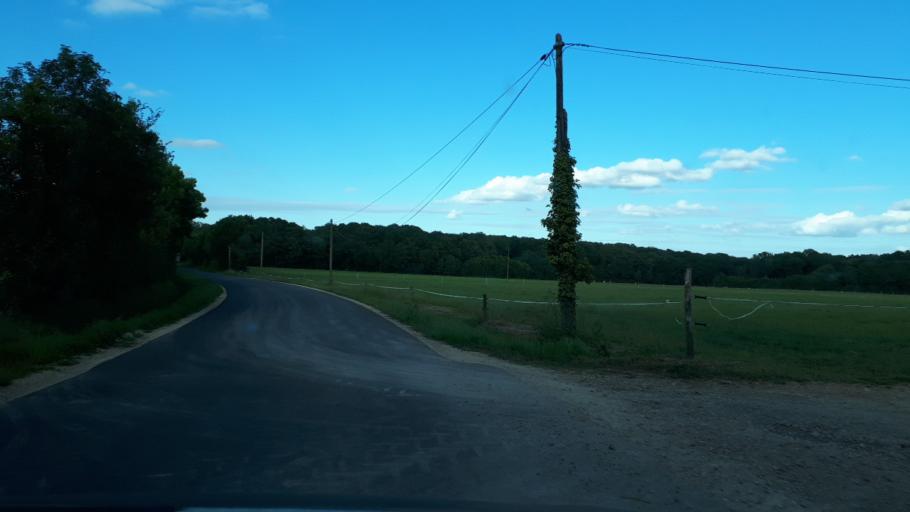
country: FR
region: Centre
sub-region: Departement du Loir-et-Cher
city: Mondoubleau
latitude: 47.9287
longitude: 0.9069
